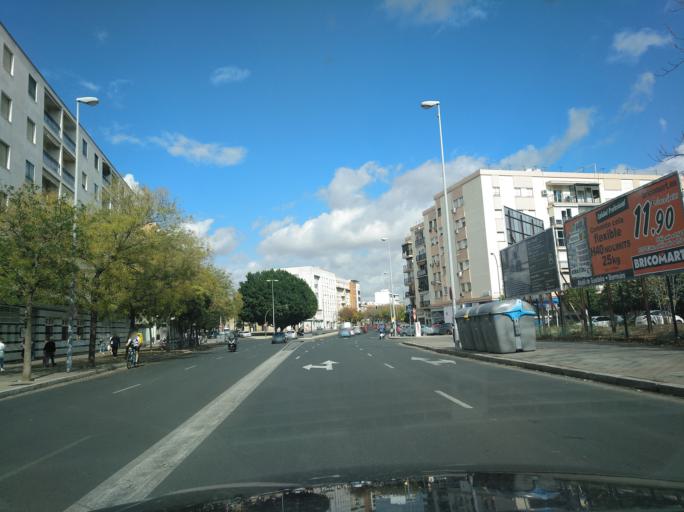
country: ES
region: Andalusia
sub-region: Provincia de Sevilla
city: Sevilla
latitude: 37.3868
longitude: -5.9831
